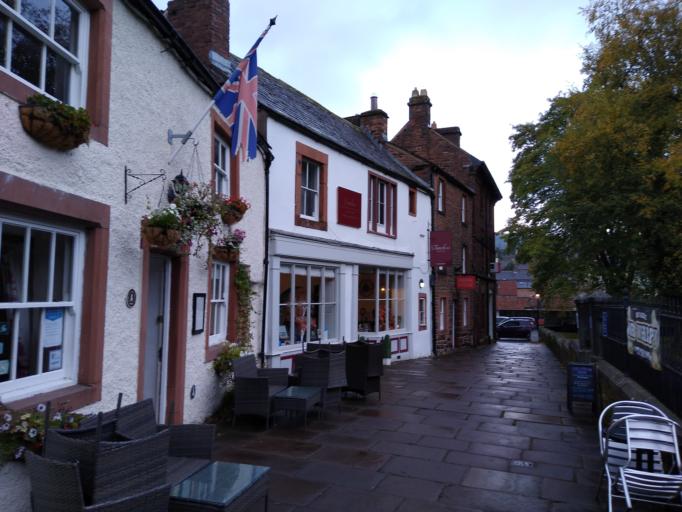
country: GB
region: England
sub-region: Cumbria
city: Penrith
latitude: 54.6645
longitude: -2.7511
